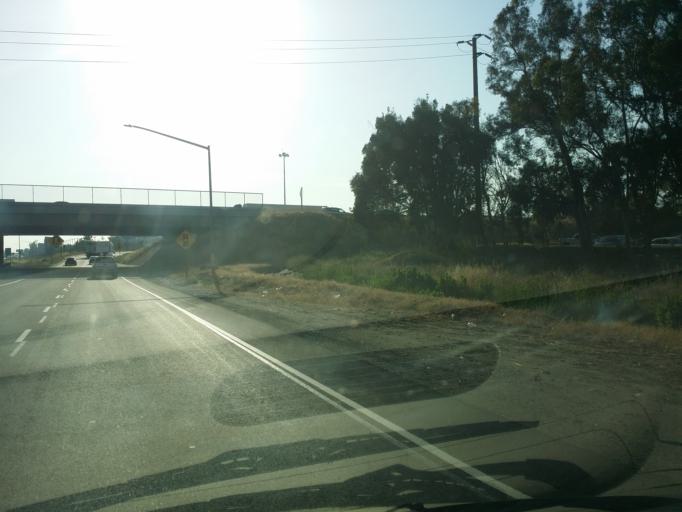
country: US
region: California
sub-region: San Bernardino County
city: Rancho Cucamonga
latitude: 34.0678
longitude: -117.5570
